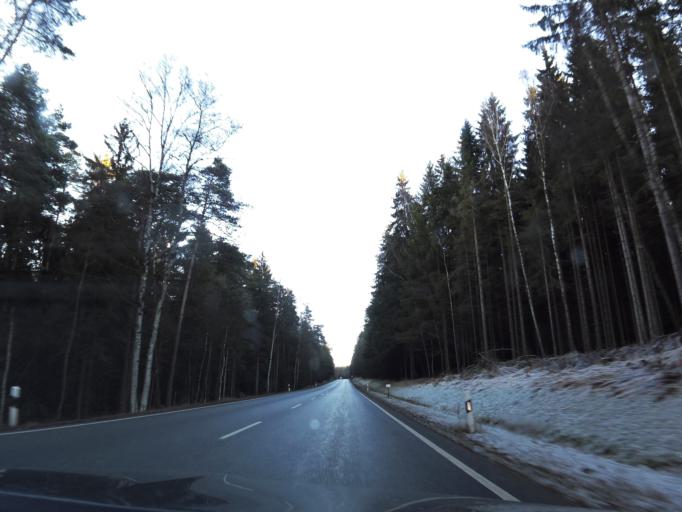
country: DE
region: Bavaria
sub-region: Upper Franconia
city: Trostau
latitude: 50.0176
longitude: 11.9752
